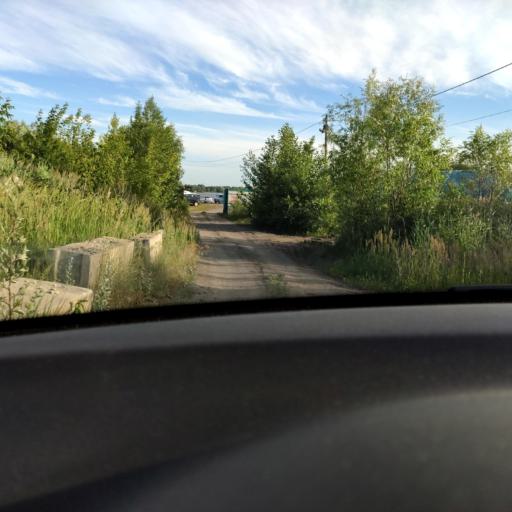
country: RU
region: Samara
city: Samara
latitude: 53.1800
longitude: 50.1085
